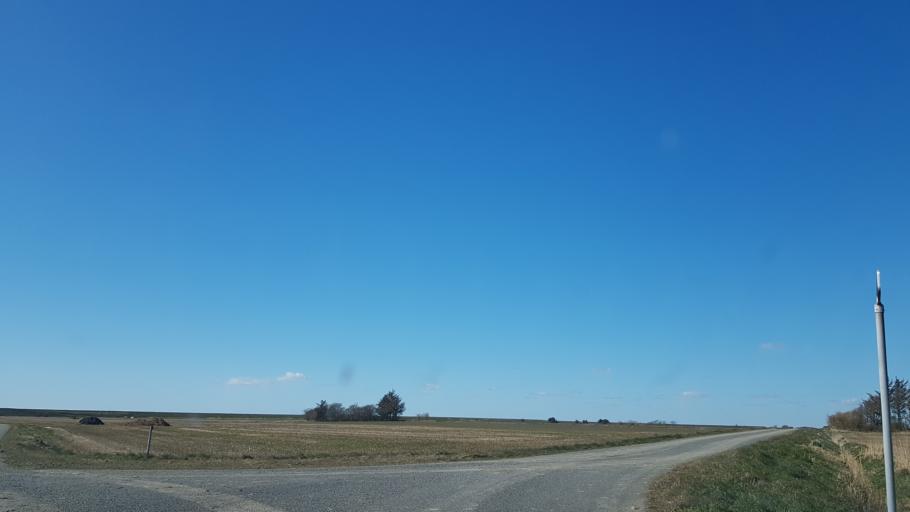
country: DK
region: South Denmark
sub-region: Esbjerg Kommune
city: Ribe
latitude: 55.2579
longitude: 8.6740
